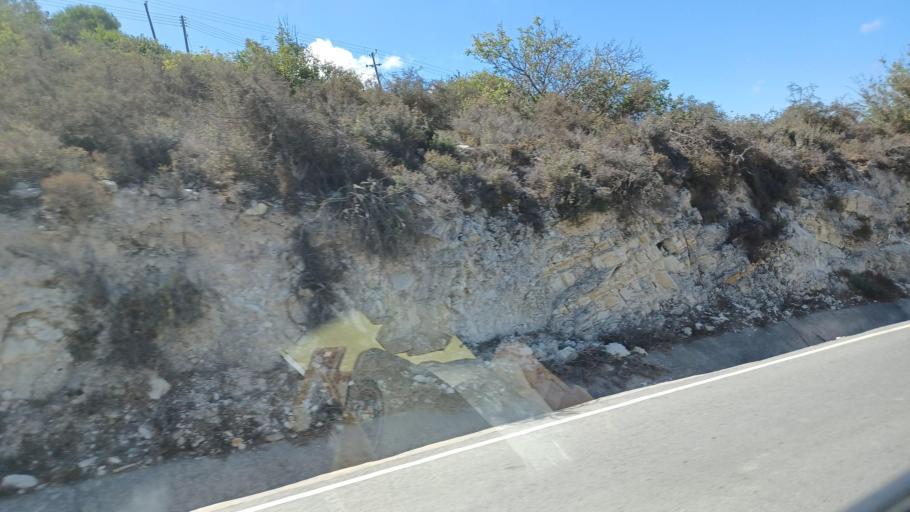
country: CY
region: Pafos
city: Tala
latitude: 34.8422
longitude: 32.4412
